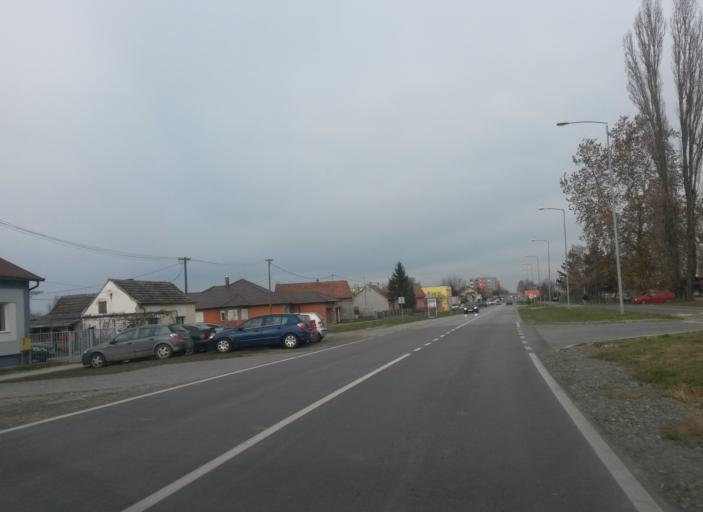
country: HR
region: Osjecko-Baranjska
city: Brijest
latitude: 45.5378
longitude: 18.6716
